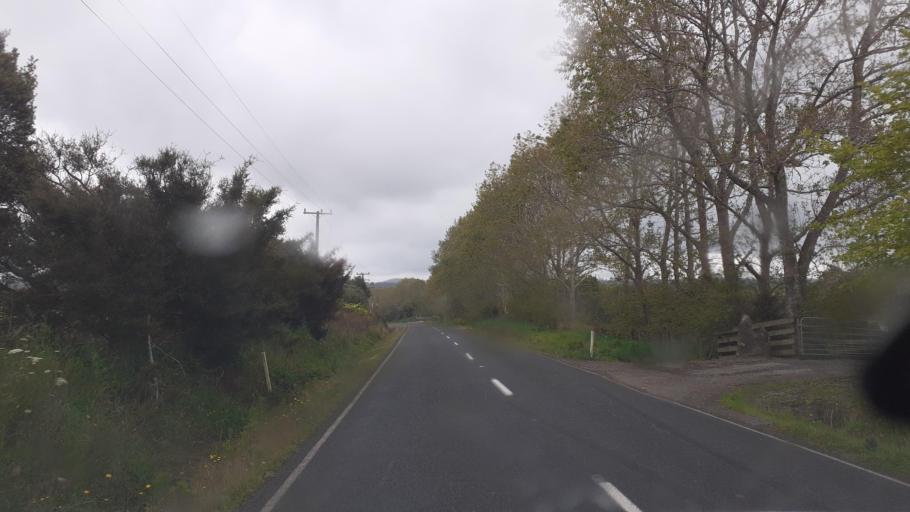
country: NZ
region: Northland
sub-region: Far North District
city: Waimate North
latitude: -35.2747
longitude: 173.8291
